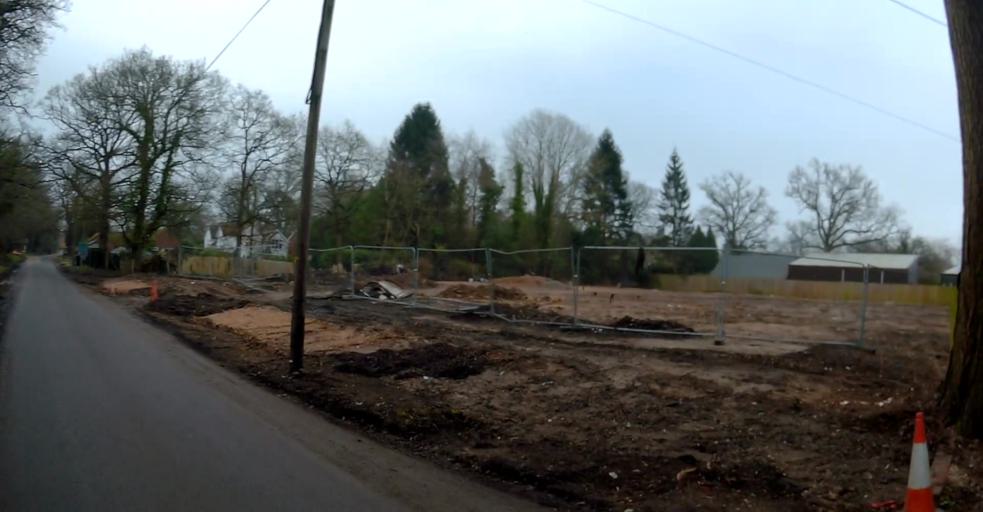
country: GB
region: England
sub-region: Hampshire
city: Eversley
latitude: 51.3628
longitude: -0.9005
